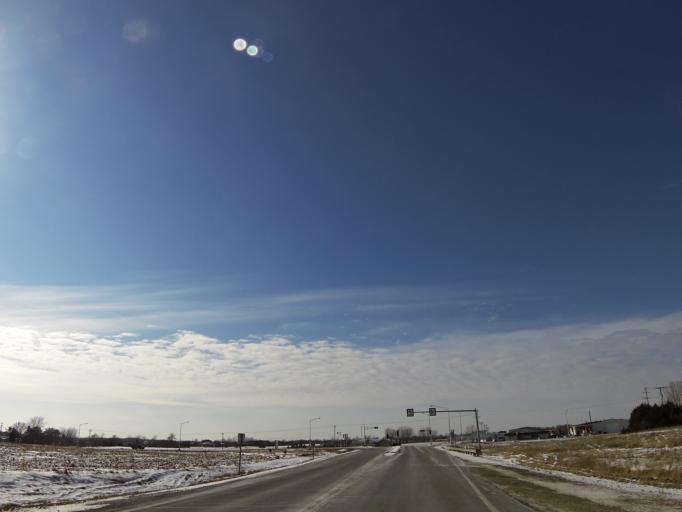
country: US
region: Wisconsin
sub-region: Saint Croix County
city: North Hudson
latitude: 44.9883
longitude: -92.6781
